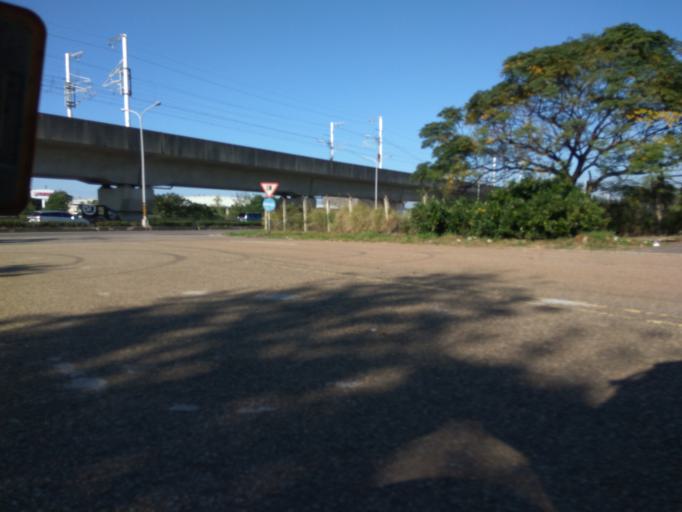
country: TW
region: Taiwan
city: Taoyuan City
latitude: 24.9727
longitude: 121.1757
